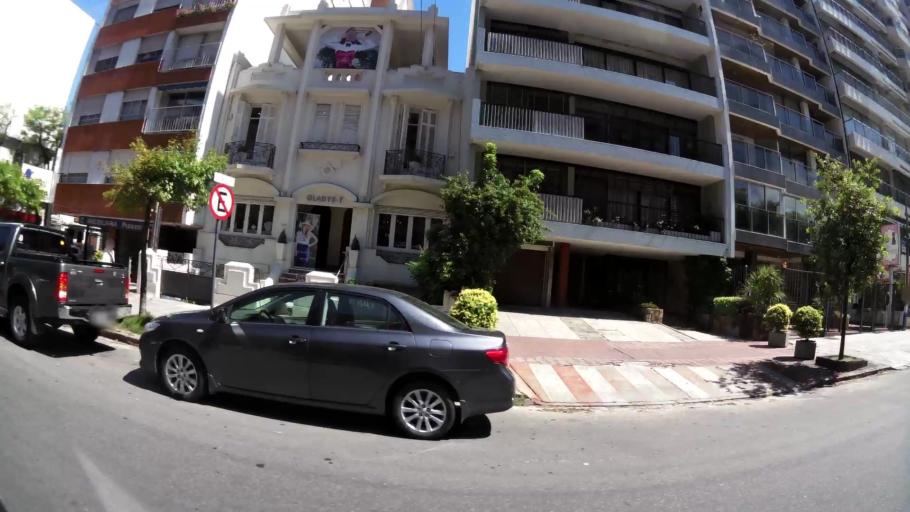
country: UY
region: Montevideo
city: Montevideo
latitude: -34.9147
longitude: -56.1519
